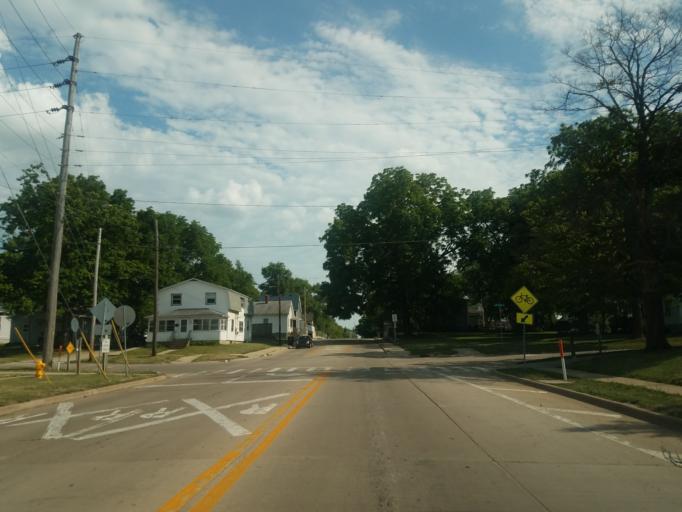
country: US
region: Illinois
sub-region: McLean County
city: Bloomington
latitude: 40.4788
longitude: -89.0066
